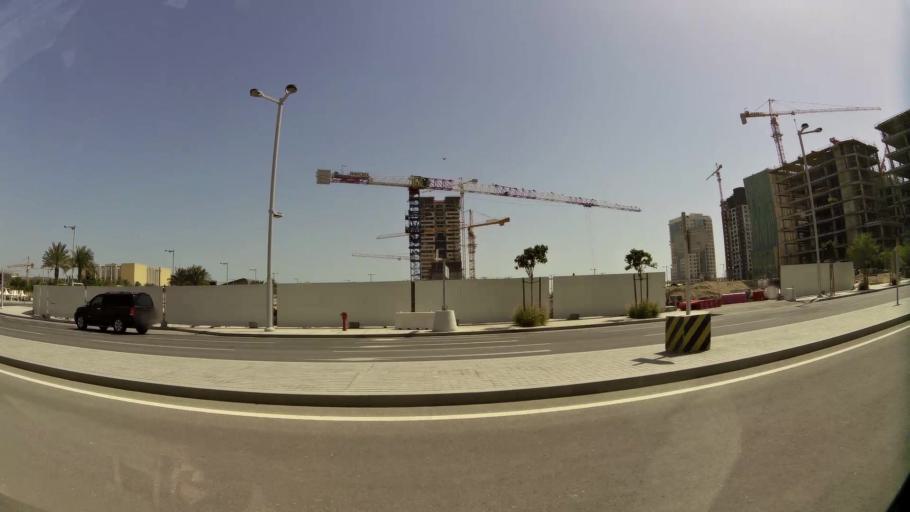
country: QA
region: Baladiyat Umm Salal
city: Umm Salal Muhammad
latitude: 25.3973
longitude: 51.5169
